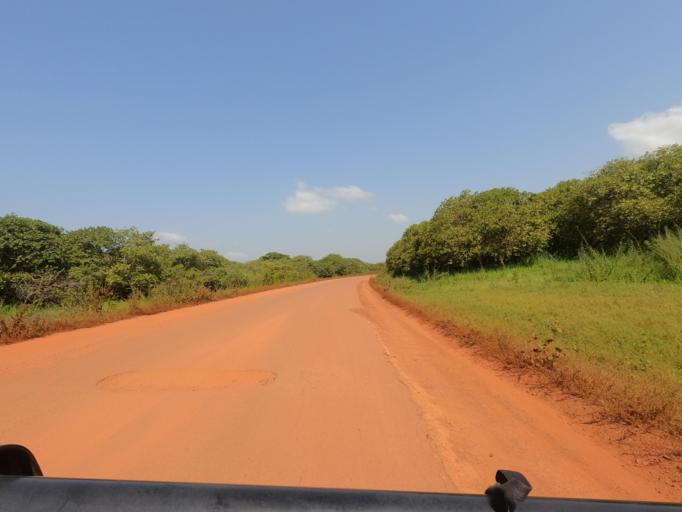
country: GW
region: Cacheu
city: Canchungo
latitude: 12.2691
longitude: -15.7881
